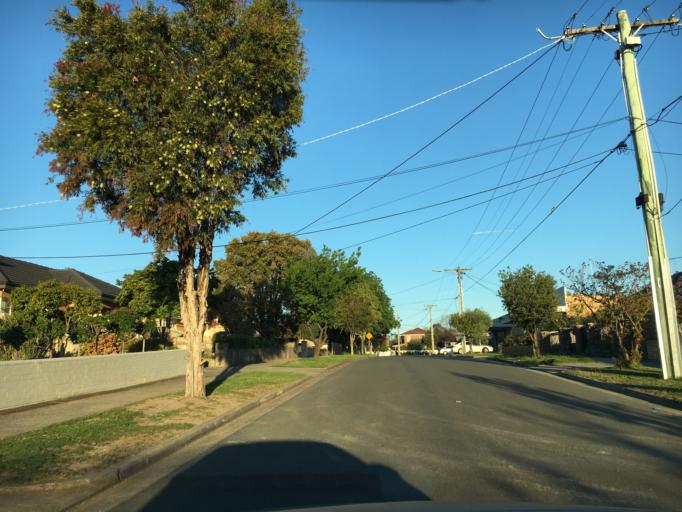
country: AU
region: Victoria
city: Clayton
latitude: -37.9073
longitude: 145.1120
